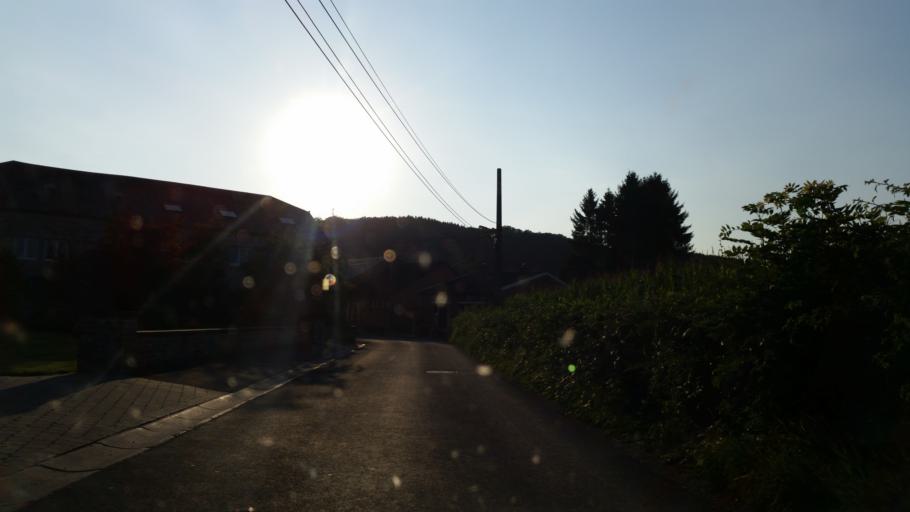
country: BE
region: Wallonia
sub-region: Province du Luxembourg
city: Durbuy
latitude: 50.3538
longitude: 5.4960
